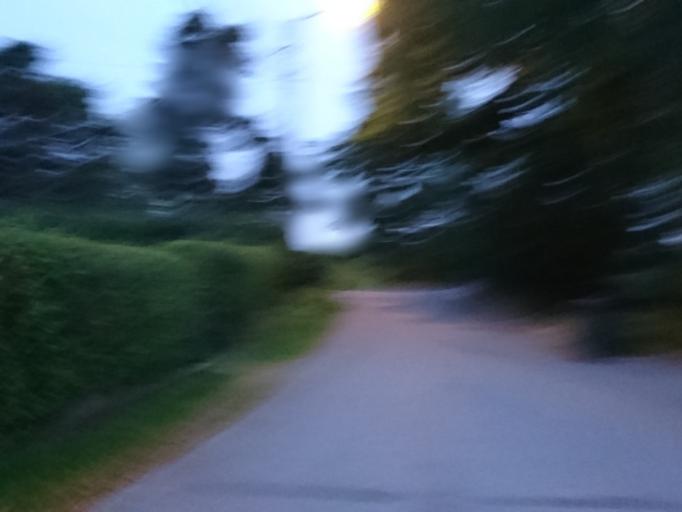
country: SE
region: Stockholm
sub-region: Huddinge Kommun
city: Segeltorp
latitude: 59.2806
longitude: 17.9398
